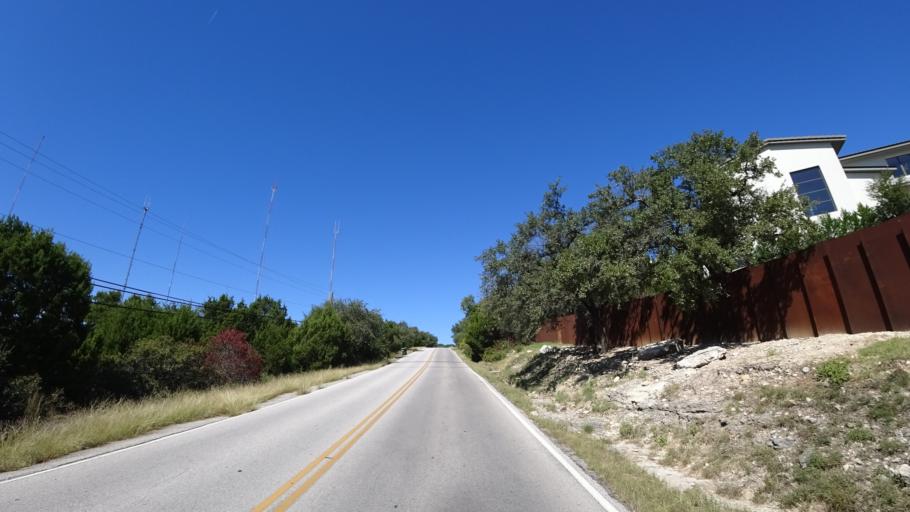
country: US
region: Texas
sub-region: Travis County
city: West Lake Hills
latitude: 30.3196
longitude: -97.7932
